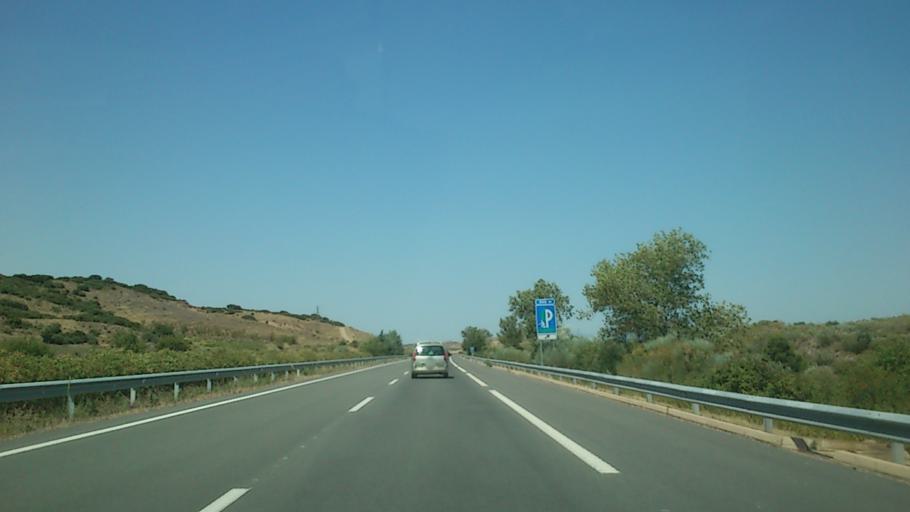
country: ES
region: La Rioja
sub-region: Provincia de La Rioja
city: Pradejon
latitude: 42.3554
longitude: -2.0595
